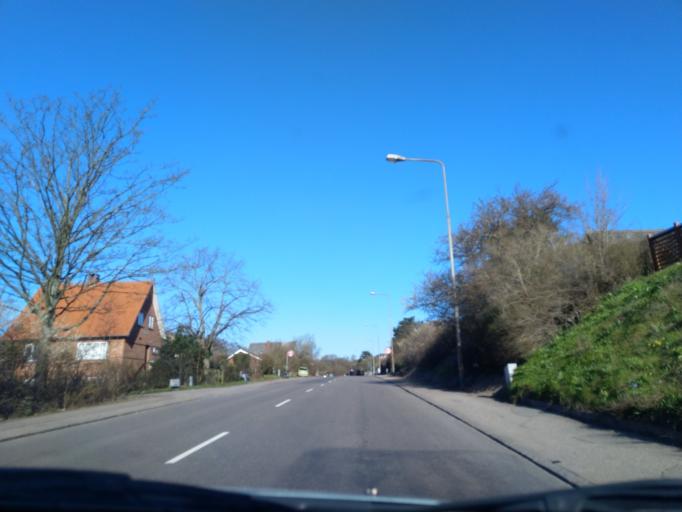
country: DK
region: Zealand
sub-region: Kalundborg Kommune
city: Kalundborg
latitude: 55.6967
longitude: 11.0425
